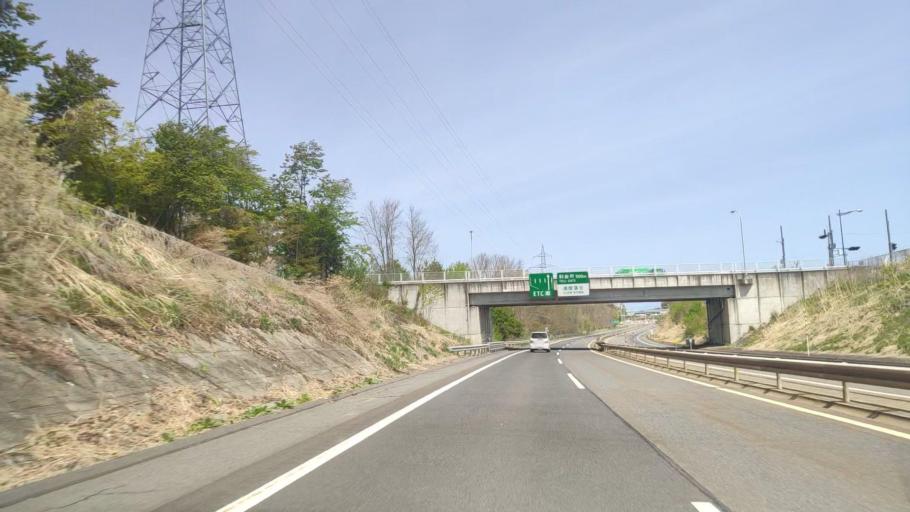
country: JP
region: Aomori
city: Hachinohe
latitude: 40.4814
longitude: 141.4598
